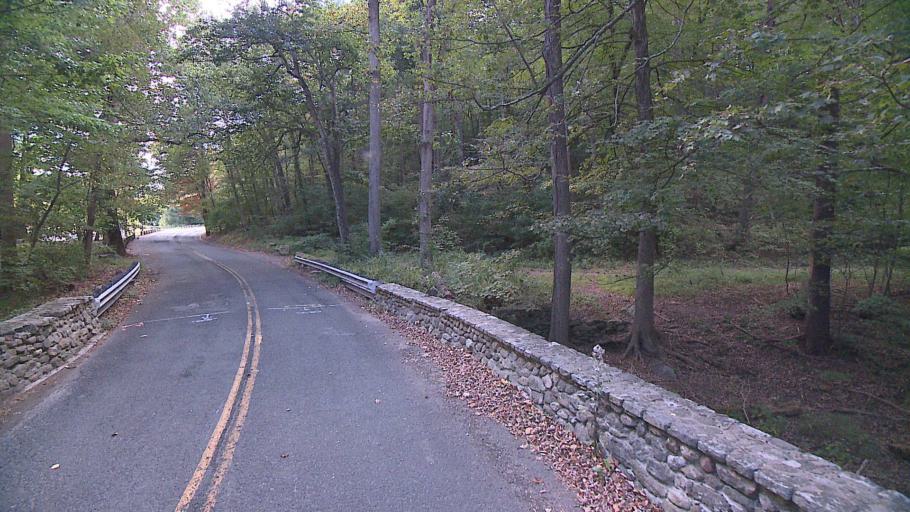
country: US
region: Connecticut
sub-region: Fairfield County
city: Shelton
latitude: 41.3388
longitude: -73.1246
